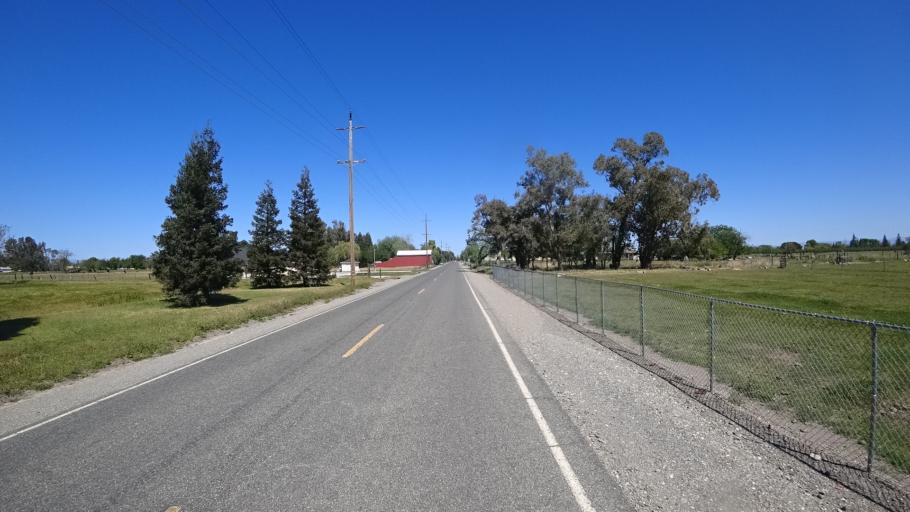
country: US
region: California
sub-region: Glenn County
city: Orland
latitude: 39.7341
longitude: -122.1782
